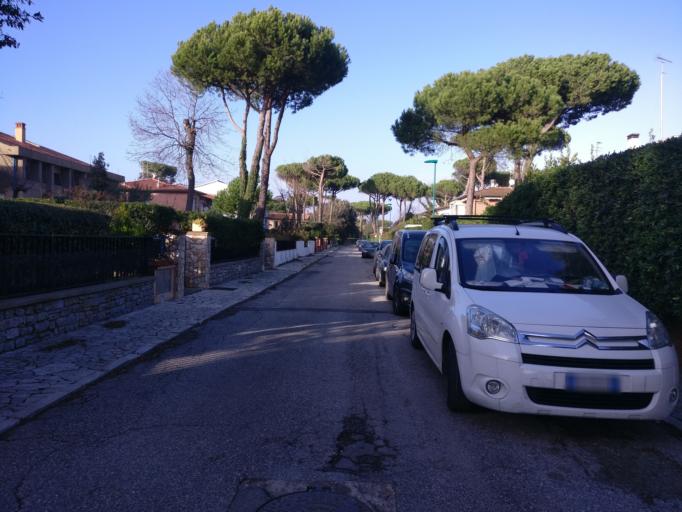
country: IT
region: Tuscany
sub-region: Province of Pisa
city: Marina di Pisa-Tirrenia-Calambrone
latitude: 43.6113
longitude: 10.2936
